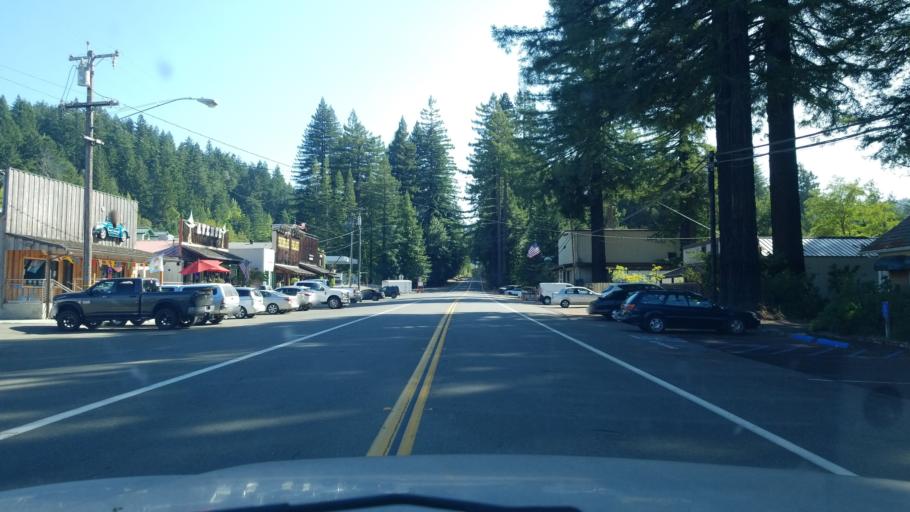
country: US
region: California
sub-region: Humboldt County
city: Redway
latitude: 40.2361
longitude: -123.8244
